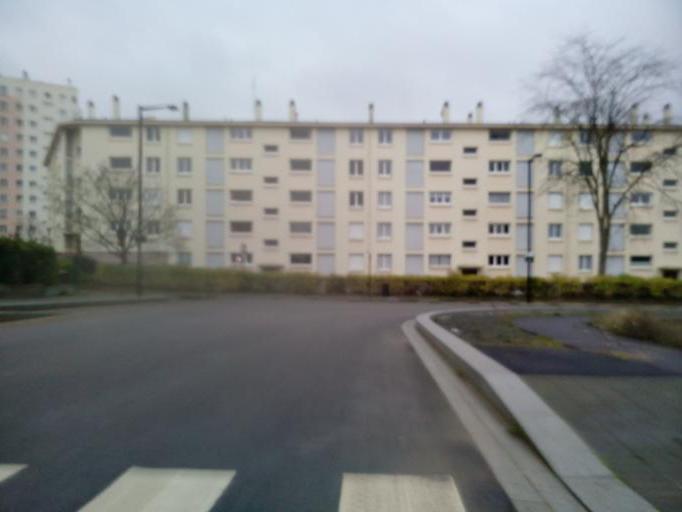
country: FR
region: Brittany
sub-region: Departement d'Ille-et-Vilaine
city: Rennes
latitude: 48.0929
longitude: -1.6971
